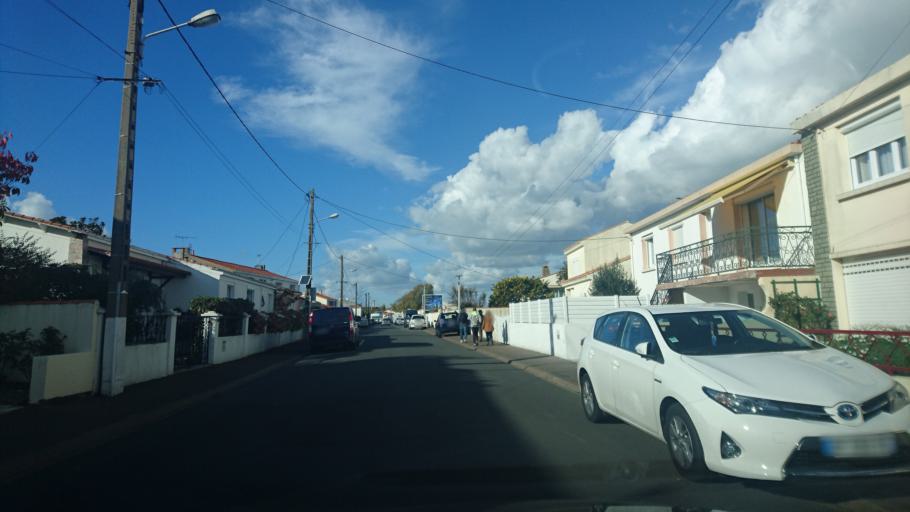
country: FR
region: Pays de la Loire
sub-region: Departement de la Vendee
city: Les Sables-d'Olonne
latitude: 46.5062
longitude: -1.8009
